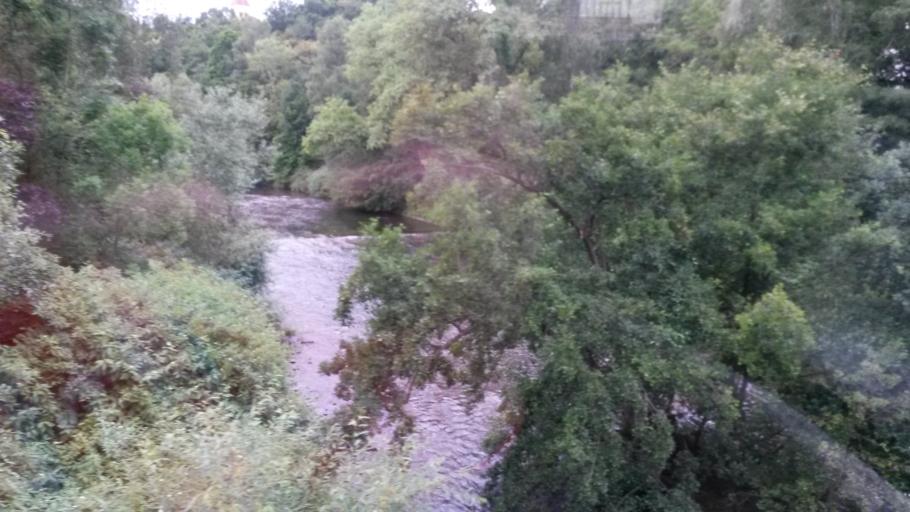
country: DE
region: Baden-Wuerttemberg
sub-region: Karlsruhe Region
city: Pforzheim
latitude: 48.8780
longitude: 8.6762
